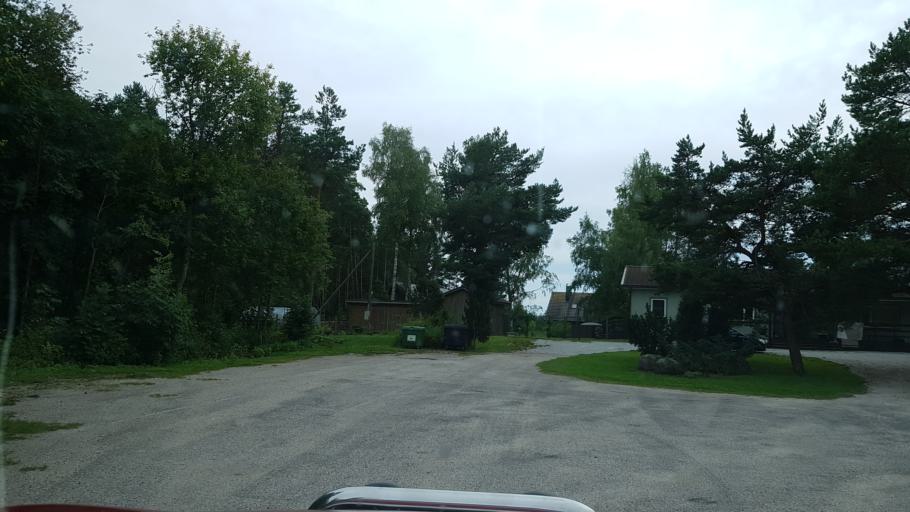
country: EE
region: Laeaene
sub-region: Ridala Parish
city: Uuemoisa
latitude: 58.9986
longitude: 23.6382
